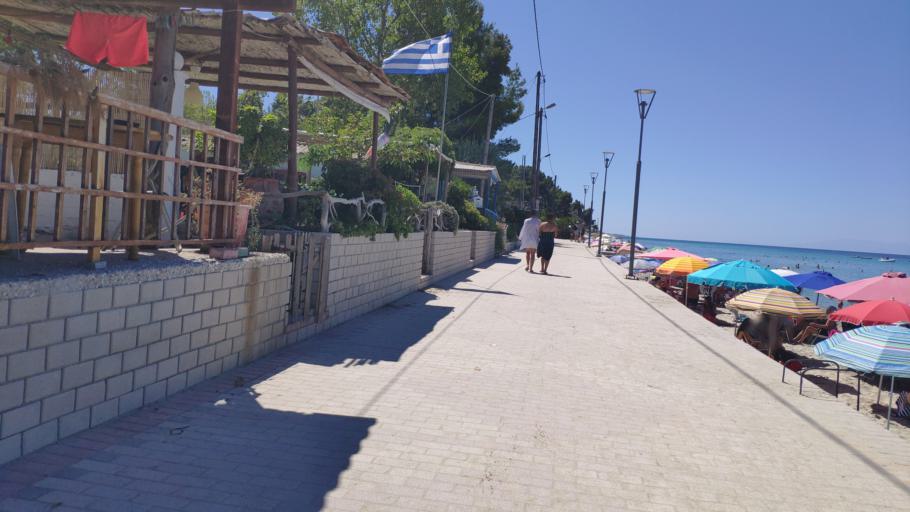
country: GR
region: Central Macedonia
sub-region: Nomos Chalkidikis
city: Kassandreia
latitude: 40.0347
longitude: 23.3600
